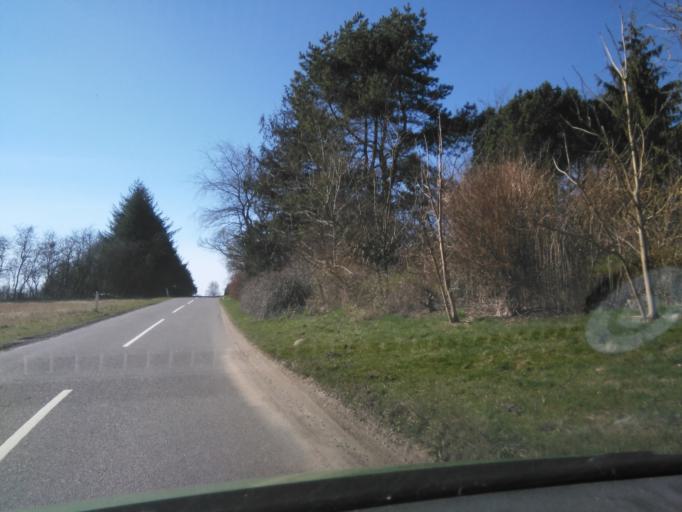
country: DK
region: Central Jutland
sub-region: Arhus Kommune
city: Trige
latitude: 56.2427
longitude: 10.1625
